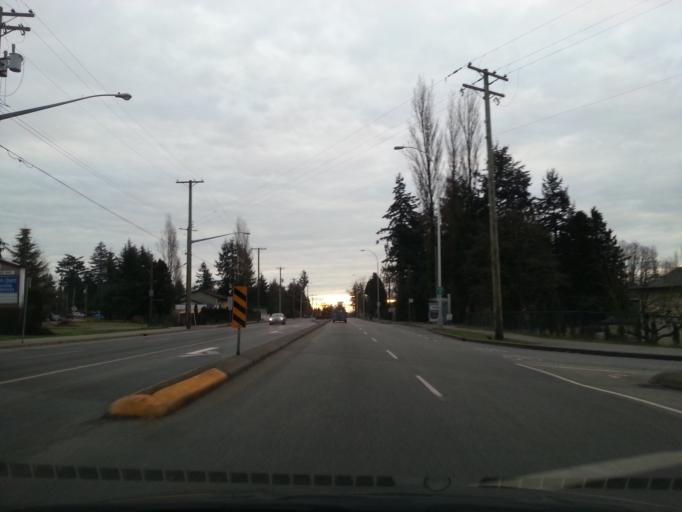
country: CA
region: British Columbia
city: Surrey
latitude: 49.1702
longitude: -122.8123
